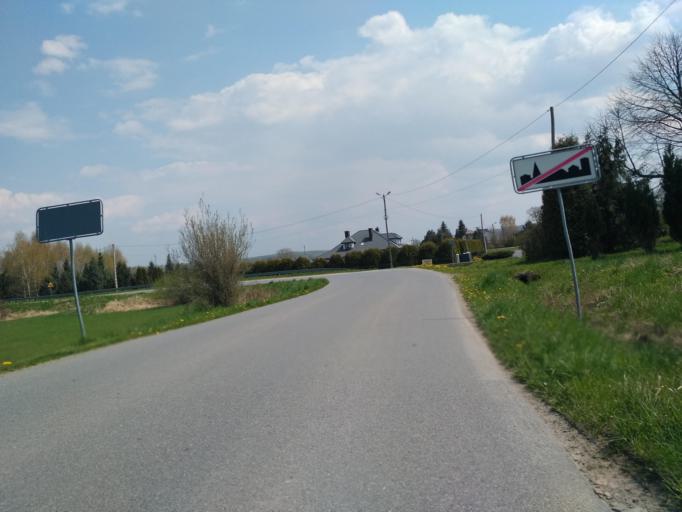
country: PL
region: Subcarpathian Voivodeship
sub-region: Powiat jasielski
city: Tarnowiec
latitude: 49.7385
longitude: 21.5421
